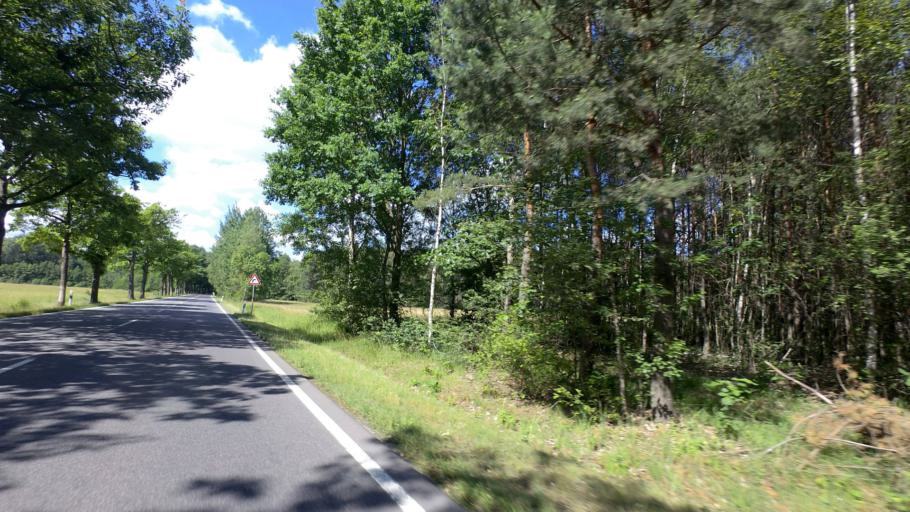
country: DE
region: Saxony
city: Hoyerswerda
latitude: 51.4437
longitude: 14.1600
